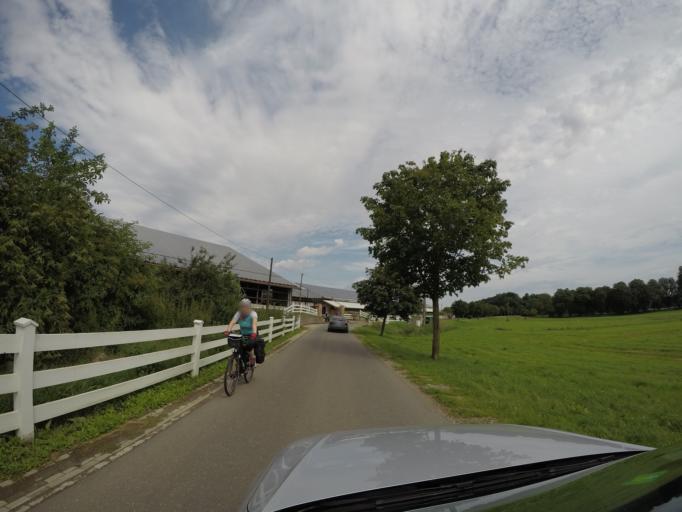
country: DE
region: Mecklenburg-Vorpommern
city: Mollenhagen
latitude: 53.4766
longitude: 12.9611
